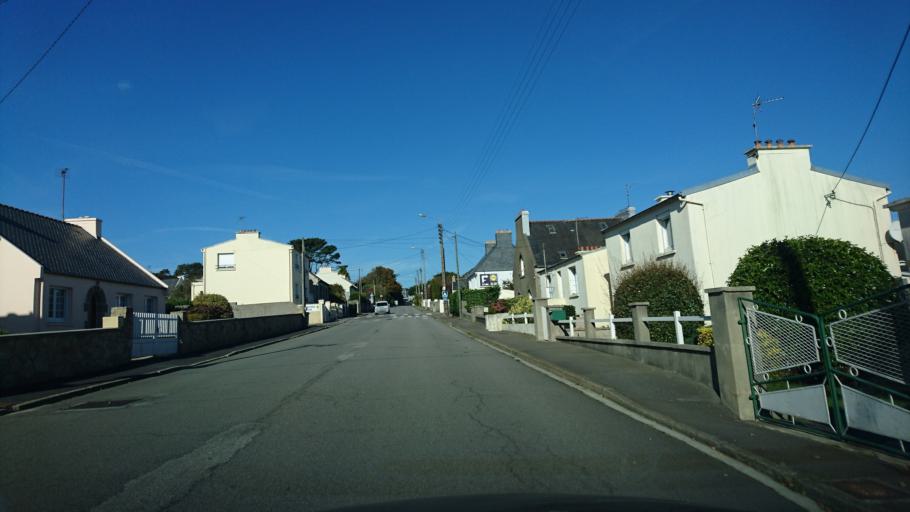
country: FR
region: Brittany
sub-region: Departement du Finistere
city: Saint-Renan
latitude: 48.4272
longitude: -4.6161
